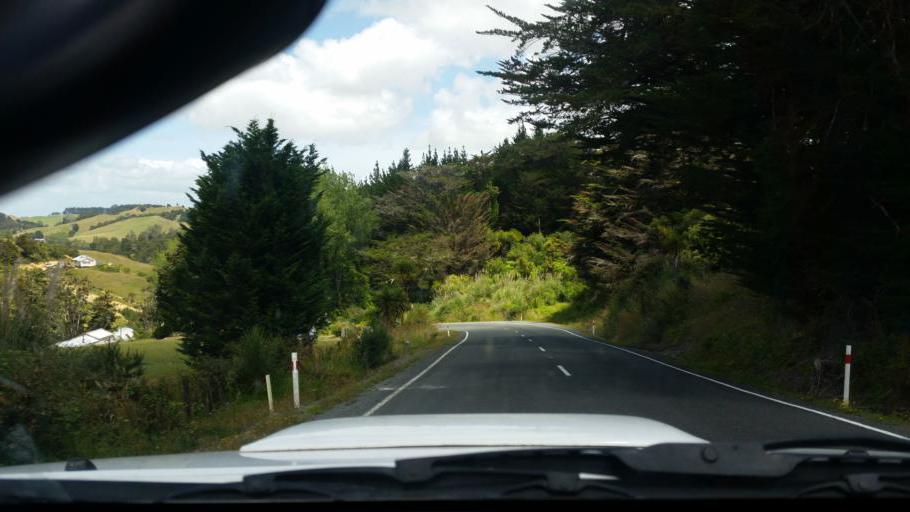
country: NZ
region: Northland
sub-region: Whangarei
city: Ruakaka
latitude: -36.0907
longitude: 174.2417
